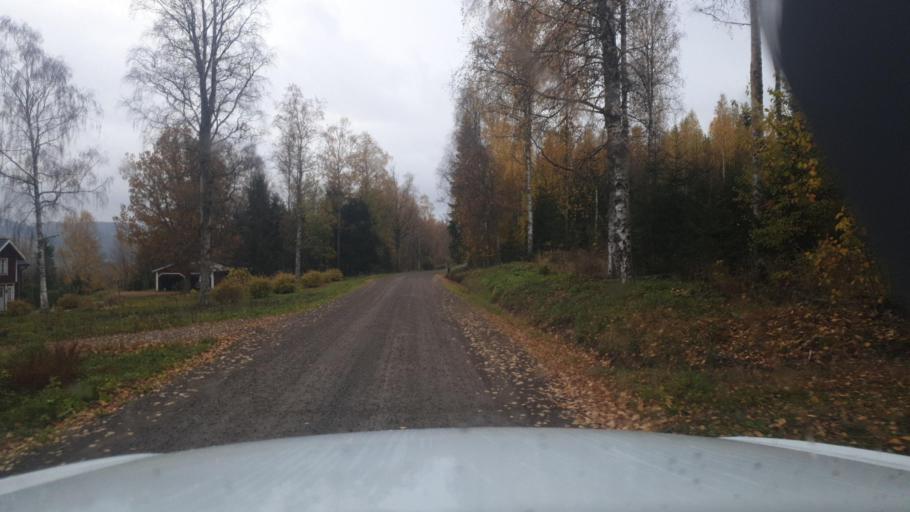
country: SE
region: Vaermland
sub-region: Torsby Kommun
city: Torsby
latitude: 59.9627
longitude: 12.8826
